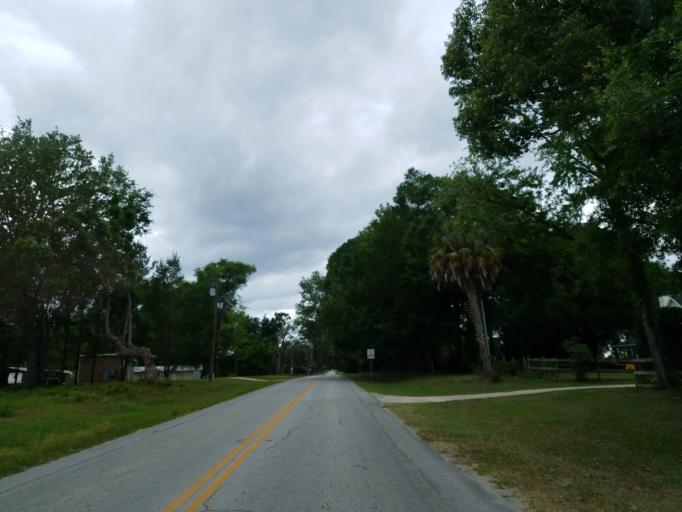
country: US
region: Florida
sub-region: Marion County
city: Ocala
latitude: 29.2958
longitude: -82.1139
